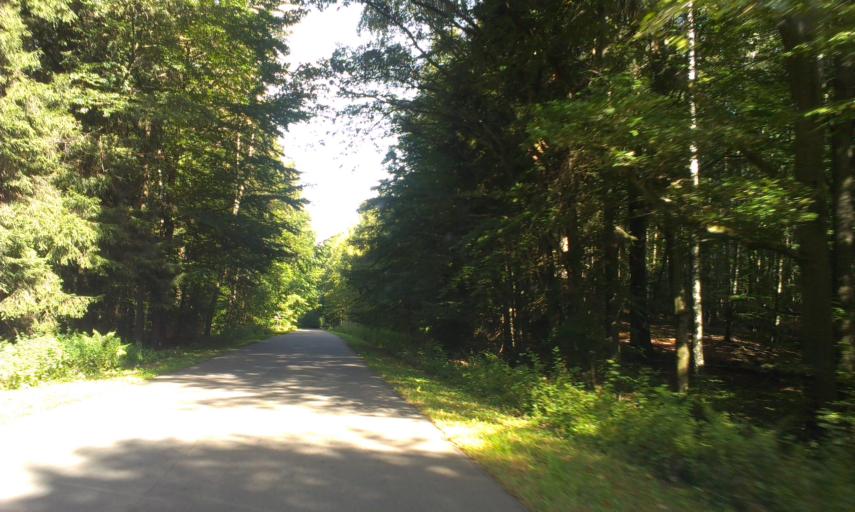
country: PL
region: West Pomeranian Voivodeship
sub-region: Powiat drawski
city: Czaplinek
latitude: 53.5914
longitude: 16.3001
